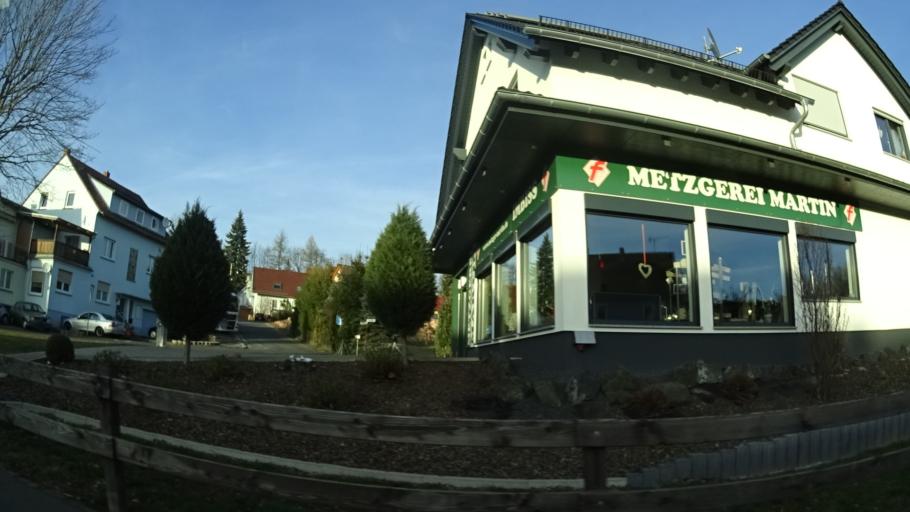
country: DE
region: Bavaria
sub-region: Regierungsbezirk Unterfranken
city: Zeitlofs
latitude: 50.3130
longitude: 9.6212
